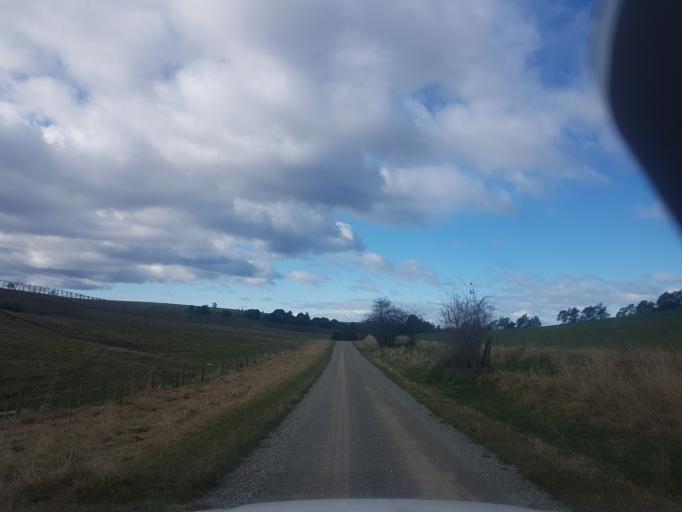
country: NZ
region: Canterbury
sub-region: Timaru District
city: Pleasant Point
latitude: -44.1839
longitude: 171.1377
